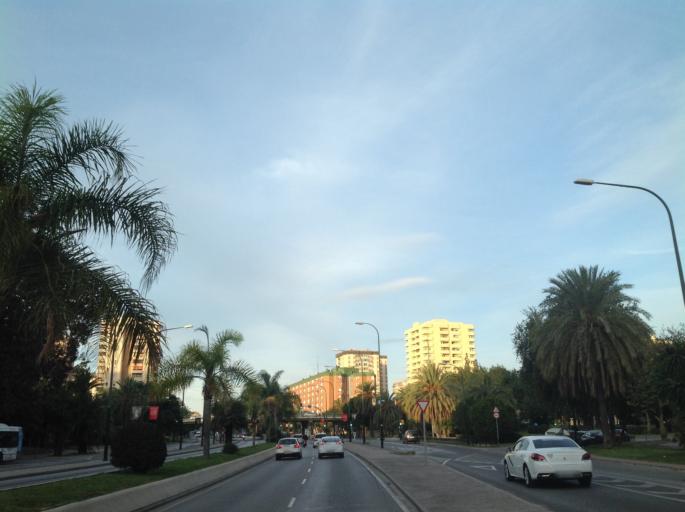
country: ES
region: Andalusia
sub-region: Provincia de Malaga
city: Malaga
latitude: 36.7172
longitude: -4.4345
